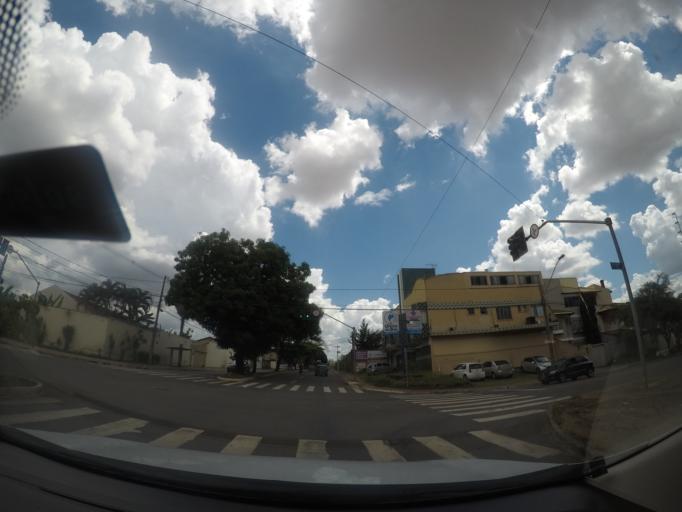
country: BR
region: Goias
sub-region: Goiania
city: Goiania
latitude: -16.6994
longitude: -49.2800
